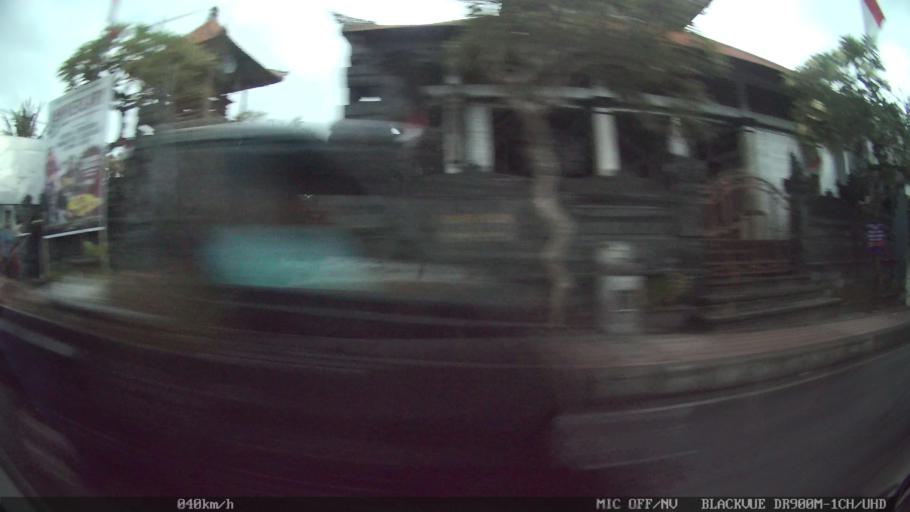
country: ID
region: Bali
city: Banjar Pasekan
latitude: -8.6067
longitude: 115.2834
